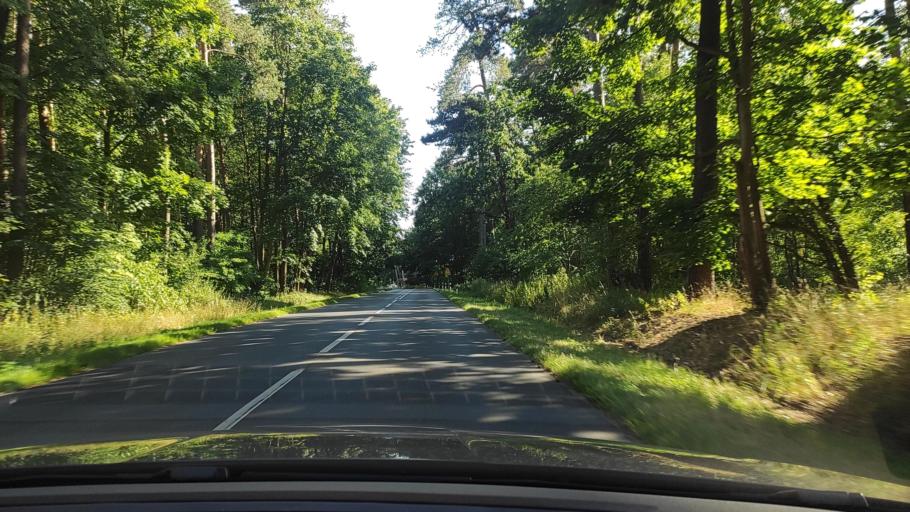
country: PL
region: Greater Poland Voivodeship
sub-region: Powiat poznanski
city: Kobylnica
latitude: 52.4491
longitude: 17.0777
